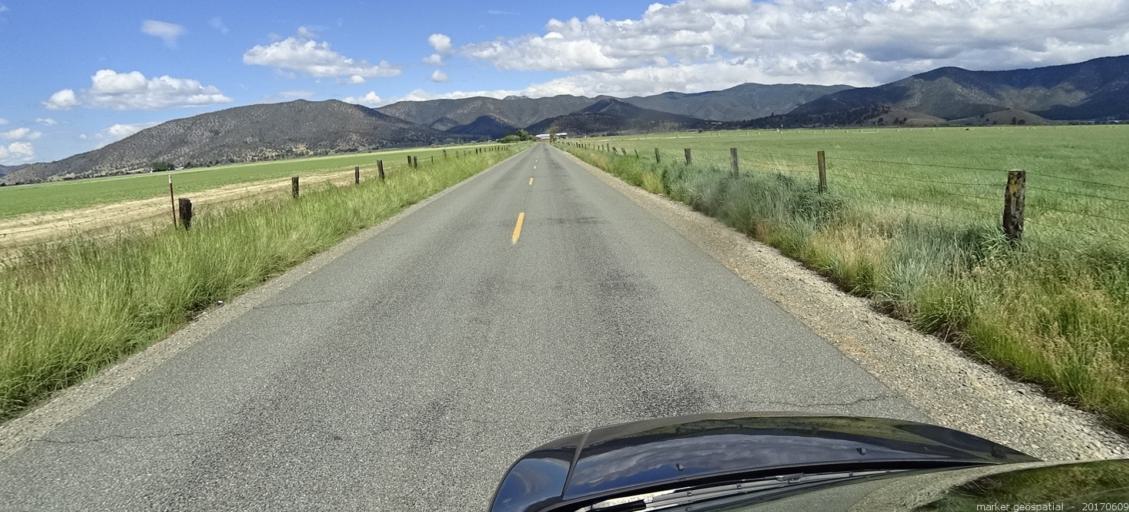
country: US
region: California
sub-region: Siskiyou County
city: Yreka
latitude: 41.4888
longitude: -122.8683
